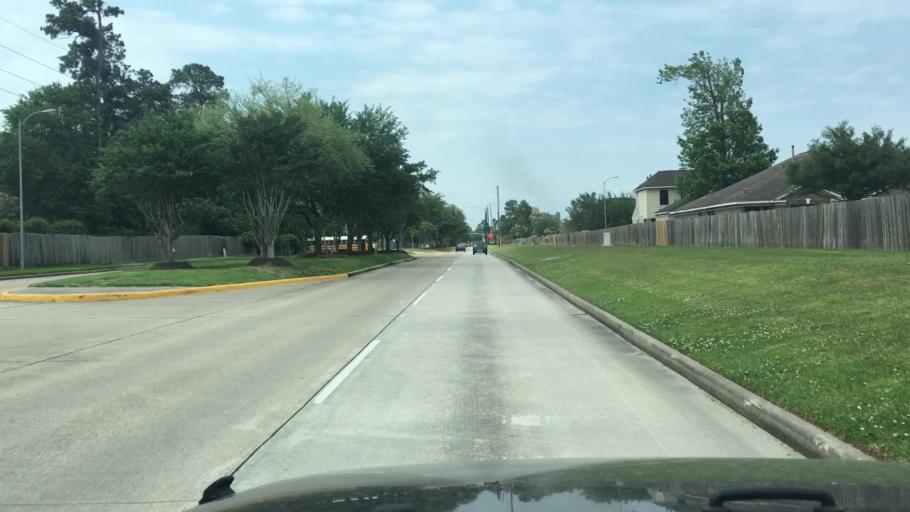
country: US
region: Texas
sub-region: Harris County
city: Atascocita
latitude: 29.9691
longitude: -95.2111
